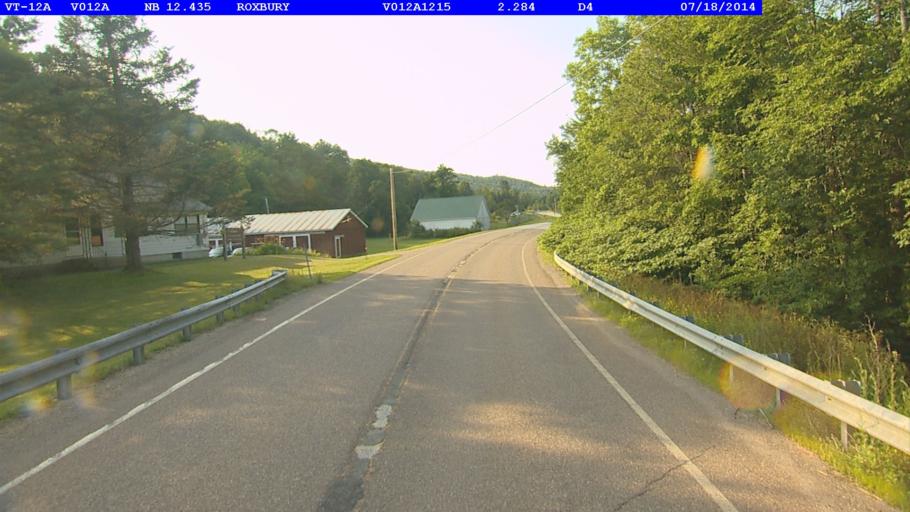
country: US
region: Vermont
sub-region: Washington County
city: Northfield
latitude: 44.0614
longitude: -72.7430
